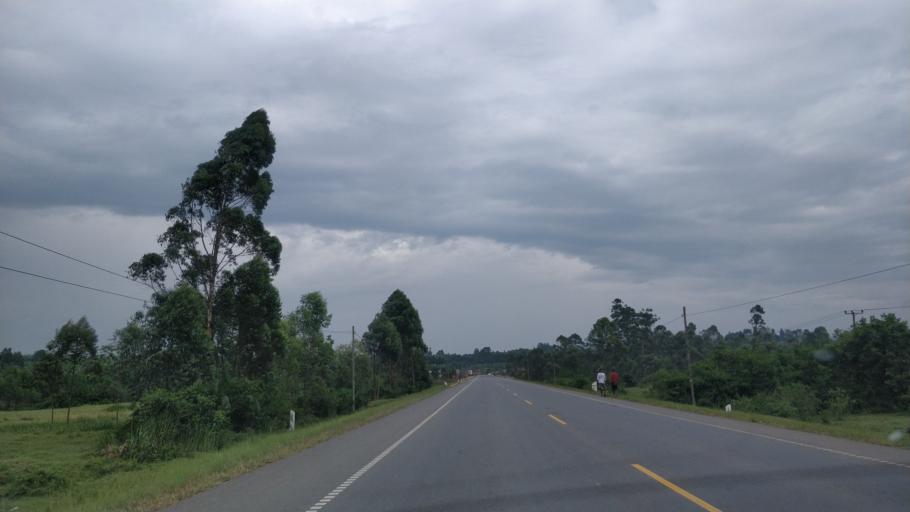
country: UG
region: Western Region
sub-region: Sheema District
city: Kibingo
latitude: -0.6691
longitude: 30.4400
